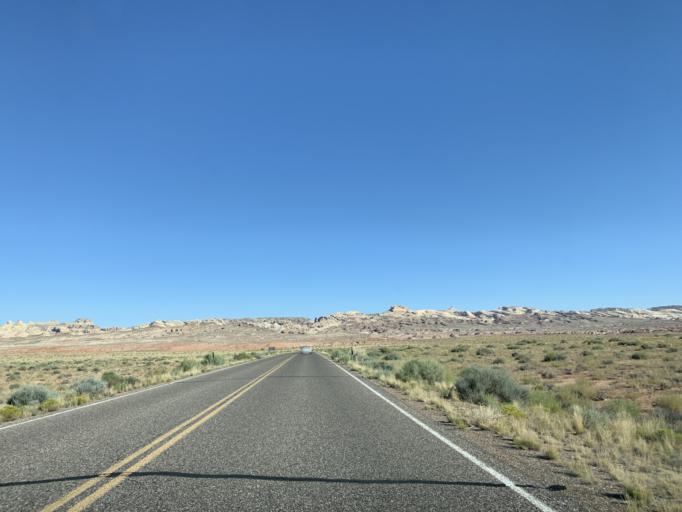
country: US
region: Utah
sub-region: Emery County
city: Ferron
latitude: 38.5790
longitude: -110.7081
